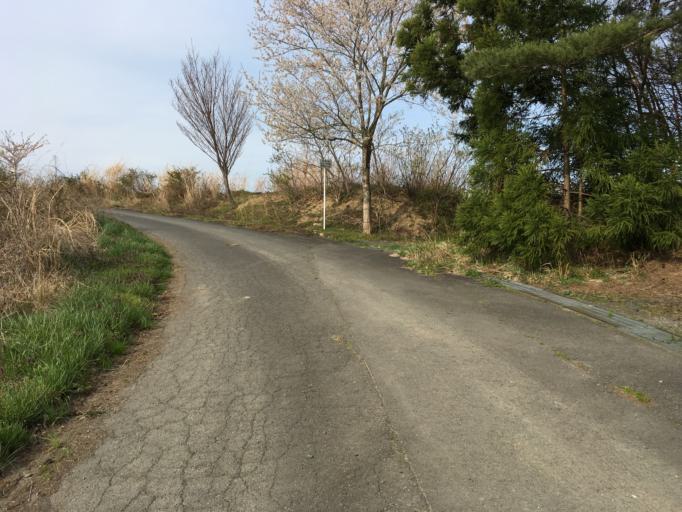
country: JP
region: Iwate
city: Ichinoseki
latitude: 38.8208
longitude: 141.2931
